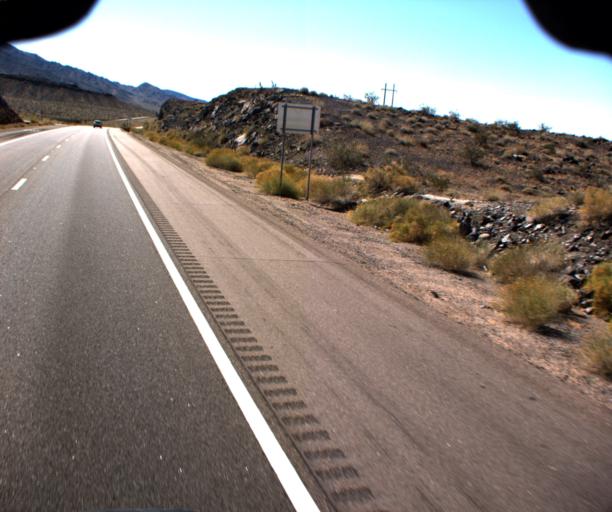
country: US
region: Nevada
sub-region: Clark County
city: Boulder City
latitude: 35.9501
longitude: -114.6488
